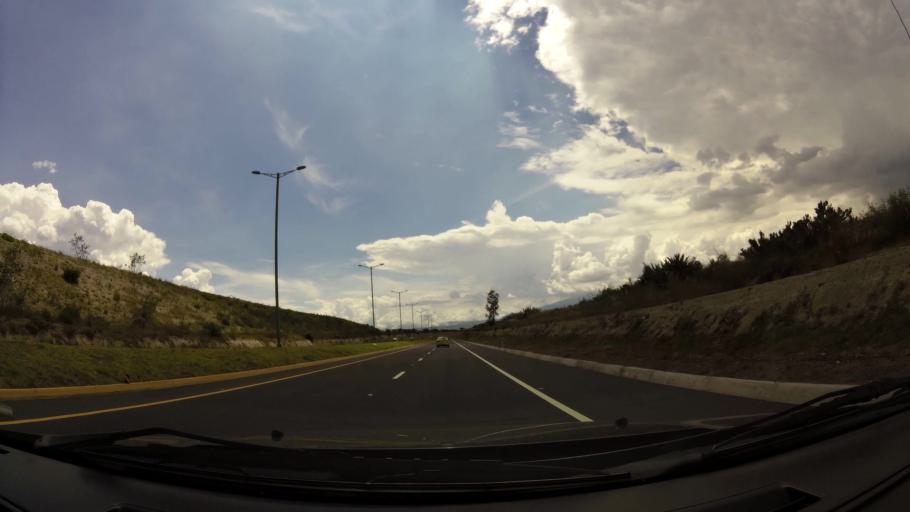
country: EC
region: Pichincha
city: Quito
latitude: -0.1049
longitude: -78.3659
